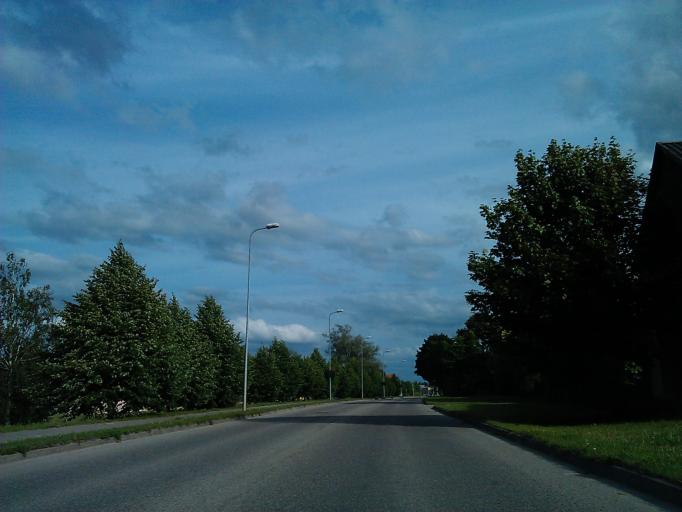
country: LV
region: Cesu Rajons
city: Cesis
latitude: 57.3016
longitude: 25.2951
